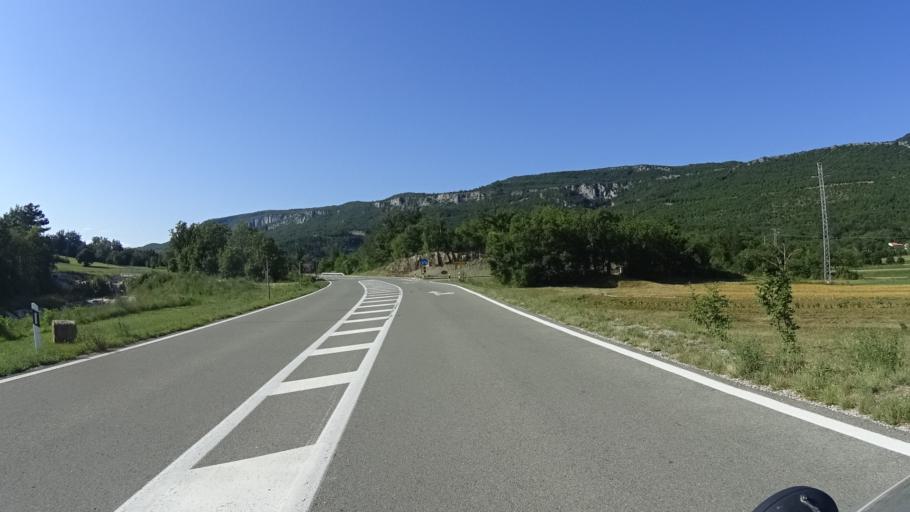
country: HR
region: Istarska
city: Lovran
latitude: 45.3181
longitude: 14.1396
